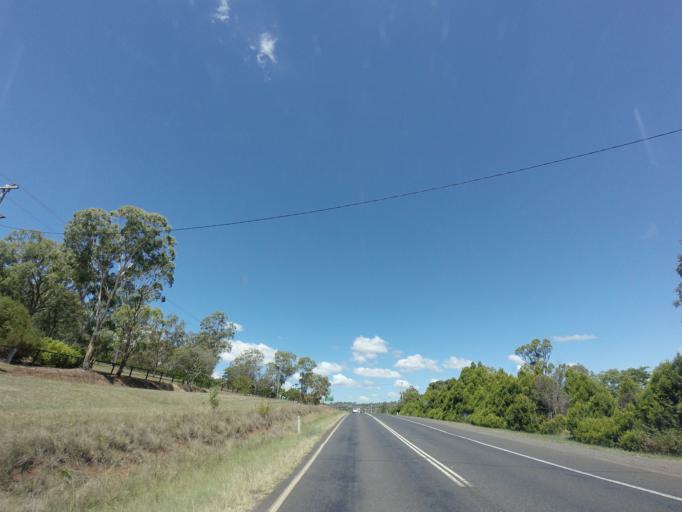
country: AU
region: Queensland
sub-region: Toowoomba
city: Westbrook
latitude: -27.6060
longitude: 151.8909
